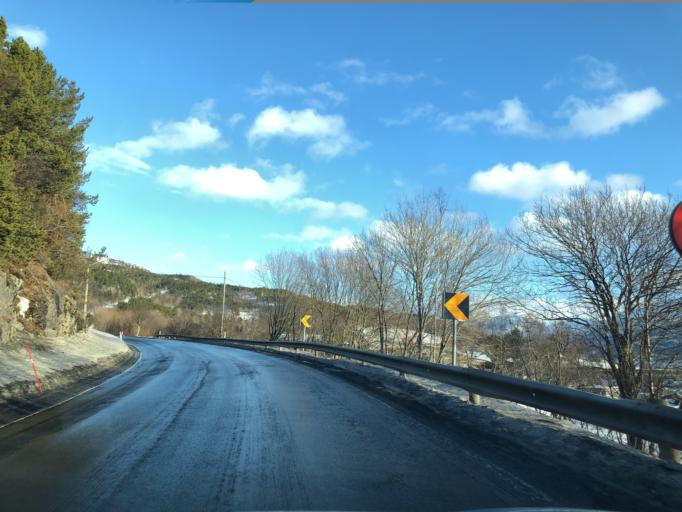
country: NO
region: Nordland
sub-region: Narvik
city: Bjerkvik
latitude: 68.4795
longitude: 17.5512
